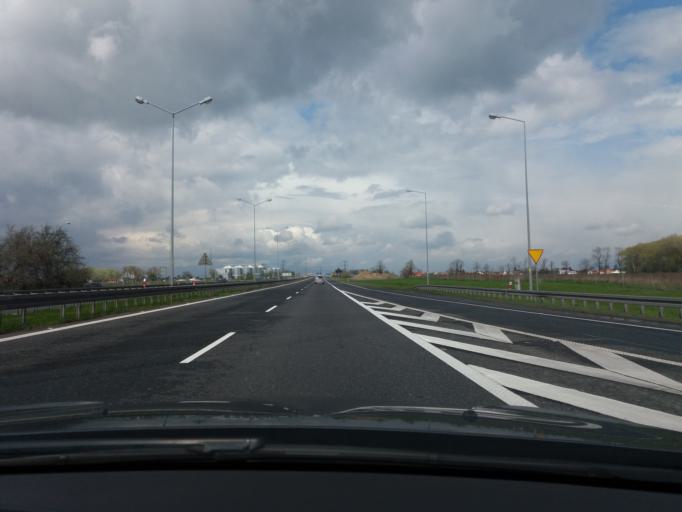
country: PL
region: Lower Silesian Voivodeship
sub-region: Powiat wroclawski
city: Zorawina
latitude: 50.9706
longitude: 17.0643
